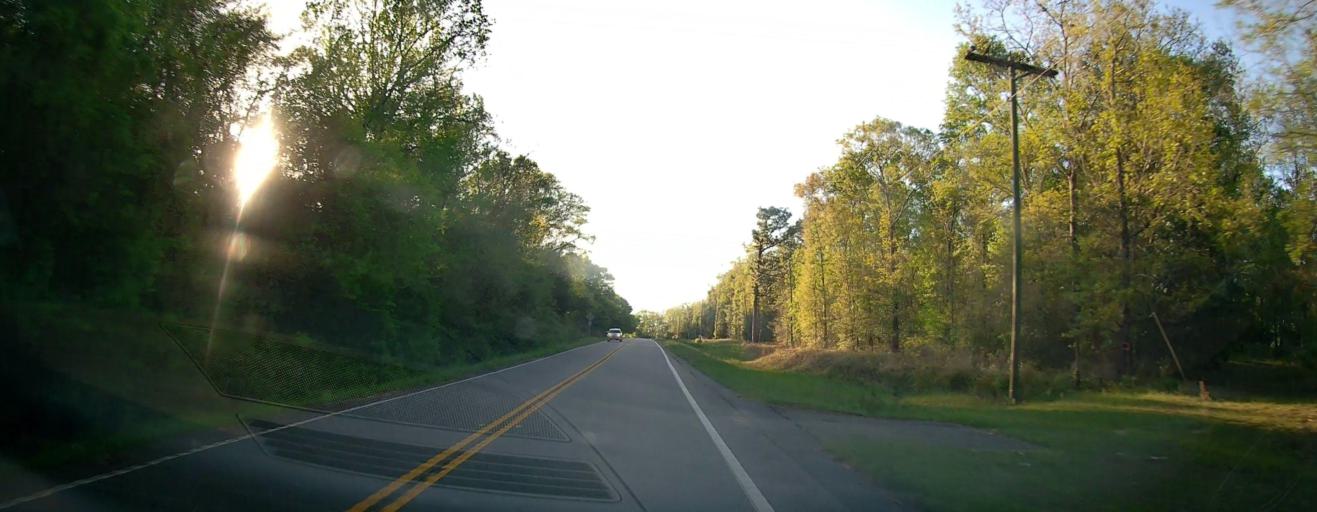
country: US
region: Georgia
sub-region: Schley County
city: Ellaville
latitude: 32.3169
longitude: -84.2561
